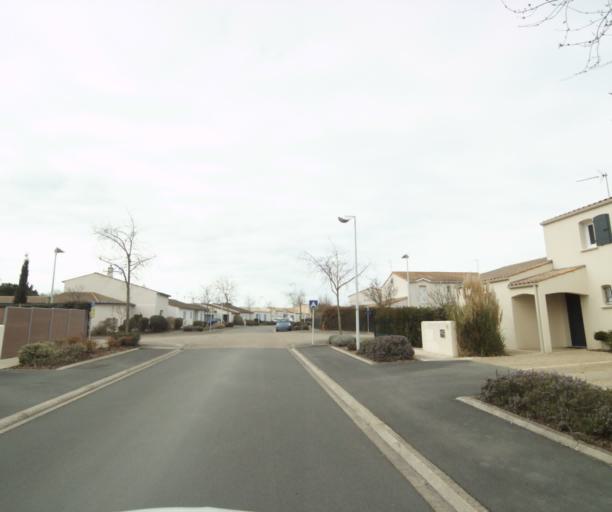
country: FR
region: Poitou-Charentes
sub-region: Departement de la Charente-Maritime
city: Lagord
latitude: 46.1846
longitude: -1.1643
